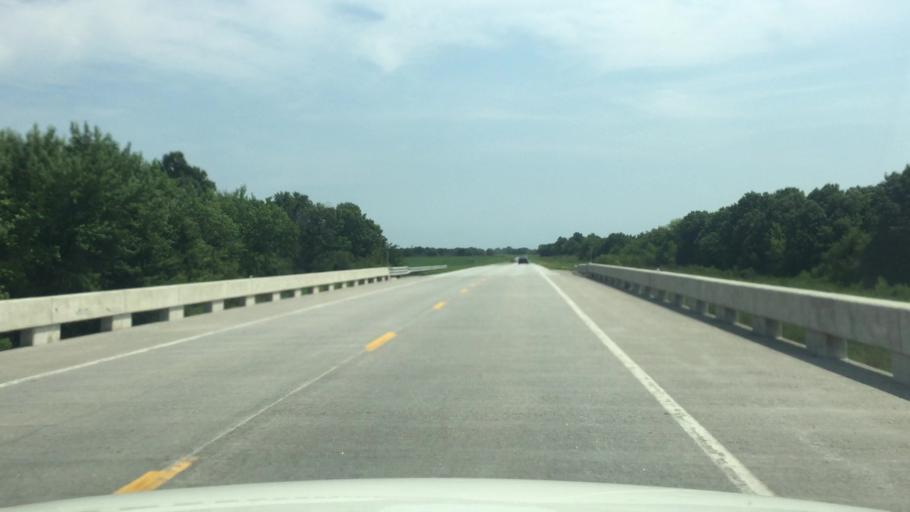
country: US
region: Kansas
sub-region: Cherokee County
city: Columbus
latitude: 37.1800
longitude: -94.9738
